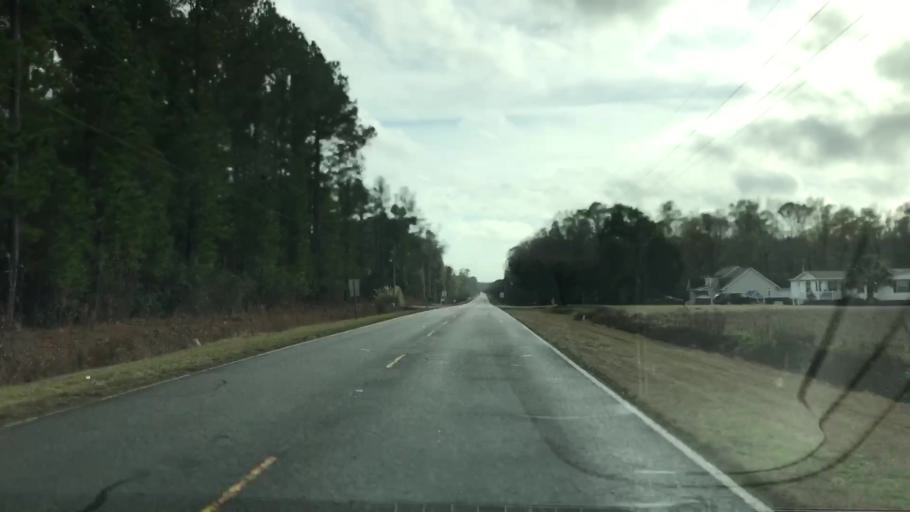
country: US
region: South Carolina
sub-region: Williamsburg County
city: Andrews
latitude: 33.4366
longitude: -79.5924
